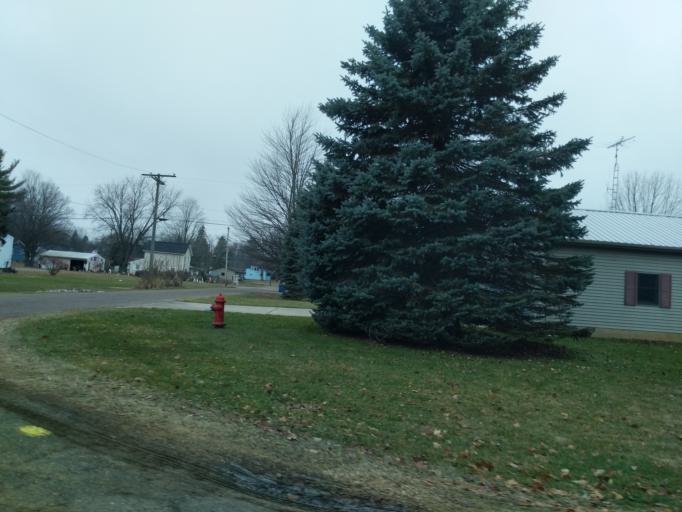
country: US
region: Michigan
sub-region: Lapeer County
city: Barnes Lake-Millers Lake
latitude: 43.3338
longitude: -83.3465
